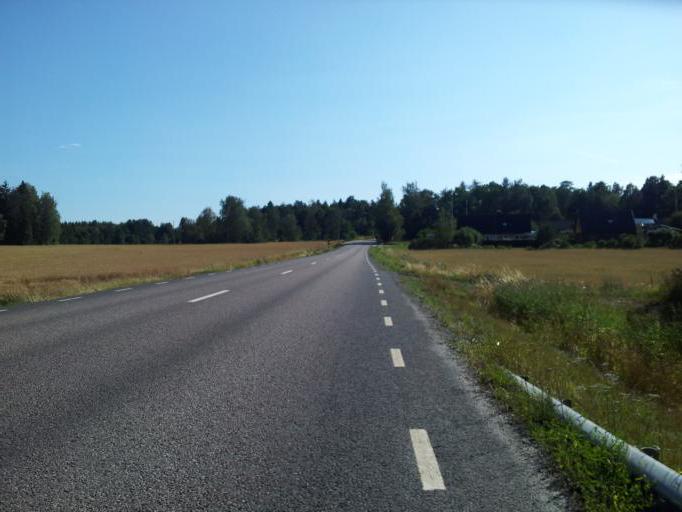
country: SE
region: Uppsala
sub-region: Knivsta Kommun
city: Knivsta
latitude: 59.8808
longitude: 17.9700
